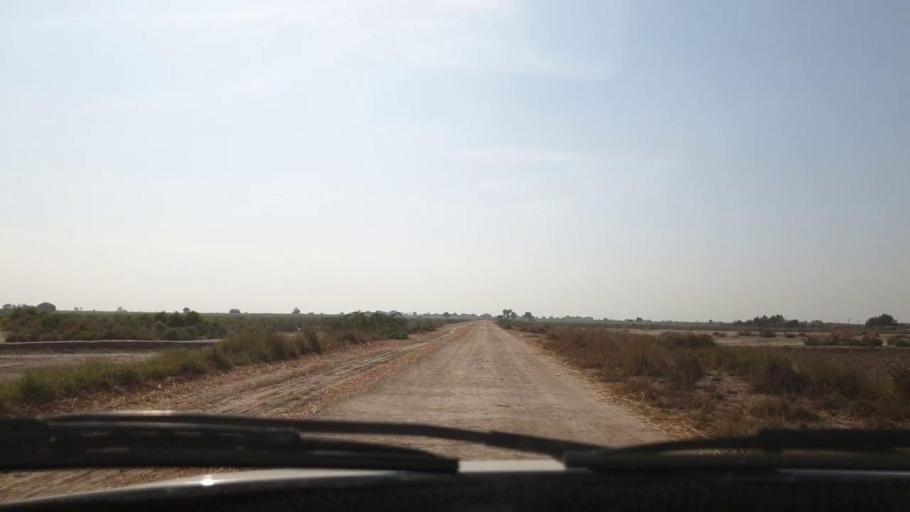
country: PK
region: Sindh
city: Bulri
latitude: 24.9498
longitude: 68.4415
